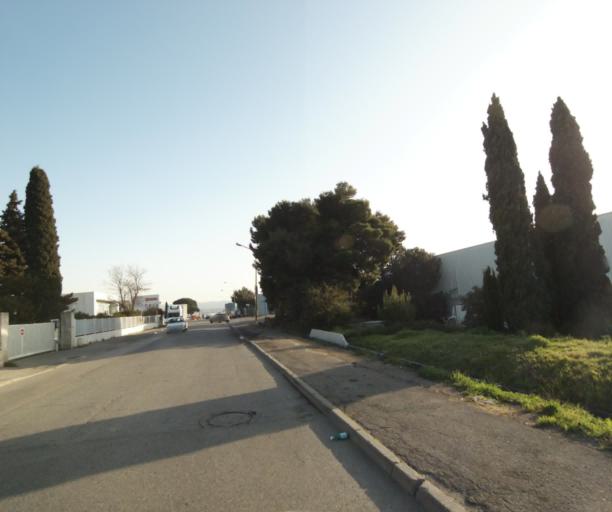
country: FR
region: Provence-Alpes-Cote d'Azur
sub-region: Departement des Bouches-du-Rhone
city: Saint-Victoret
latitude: 43.4361
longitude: 5.2393
